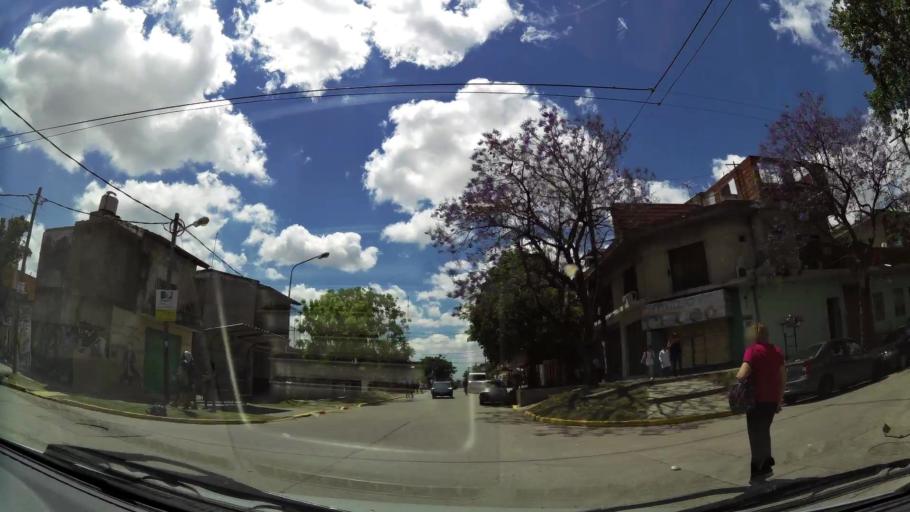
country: AR
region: Buenos Aires
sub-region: Partido de Lanus
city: Lanus
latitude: -34.6985
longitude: -58.4312
